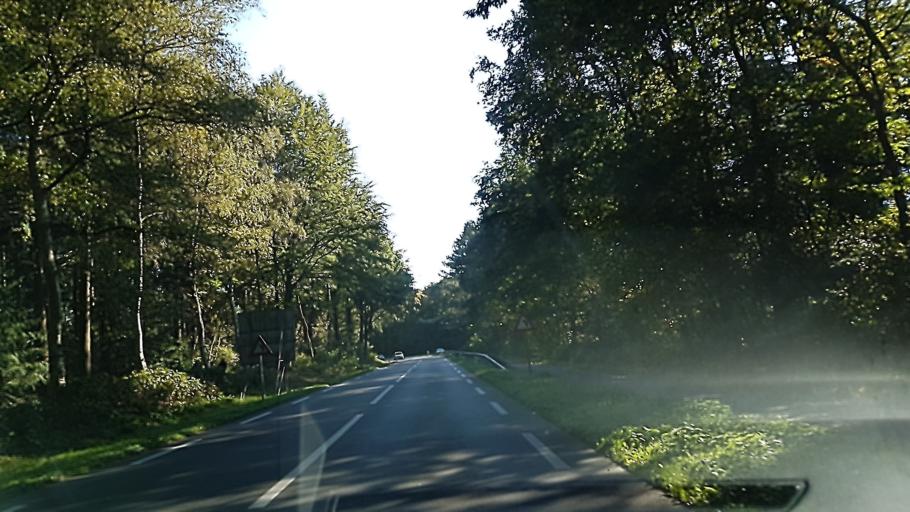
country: BE
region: Flanders
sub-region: Provincie Antwerpen
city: Stabroek
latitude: 51.3921
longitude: 4.3591
